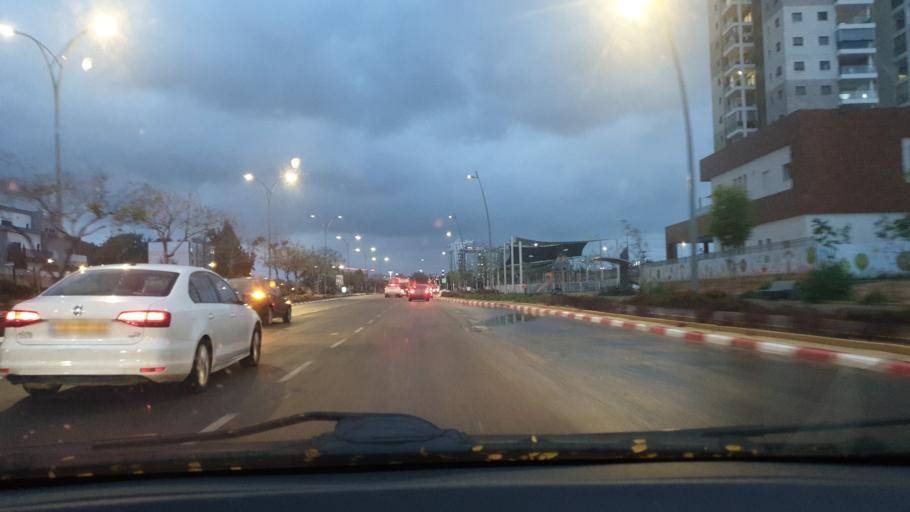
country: IL
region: Central District
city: Rishon LeZiyyon
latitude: 31.9781
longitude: 34.7970
